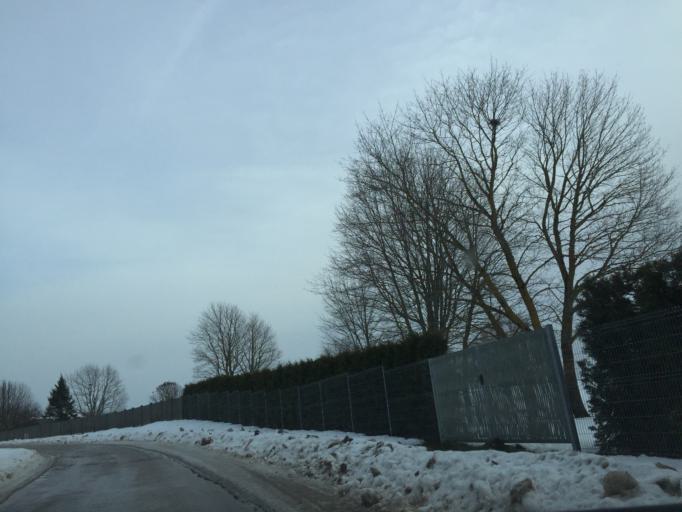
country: LV
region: Ikskile
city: Ikskile
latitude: 56.8452
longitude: 24.4436
